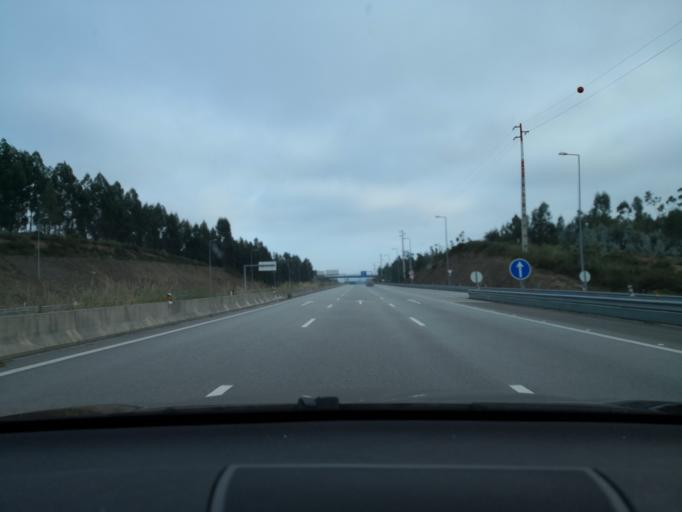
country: PT
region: Porto
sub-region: Gondomar
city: Foz do Sousa
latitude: 41.0931
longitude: -8.4566
